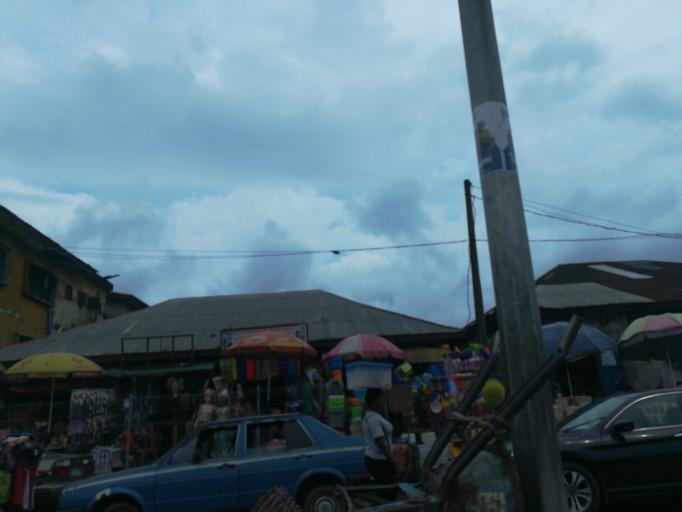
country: NG
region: Rivers
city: Port Harcourt
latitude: 4.7588
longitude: 7.0257
